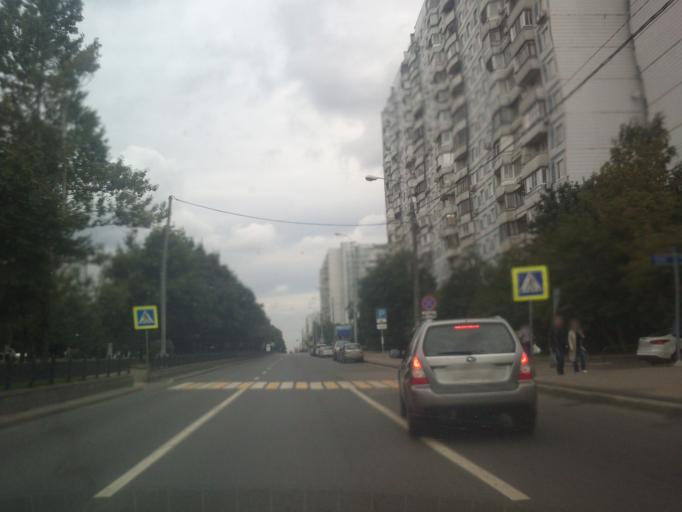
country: RU
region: Moskovskaya
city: Bol'shaya Setun'
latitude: 55.7533
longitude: 37.4091
